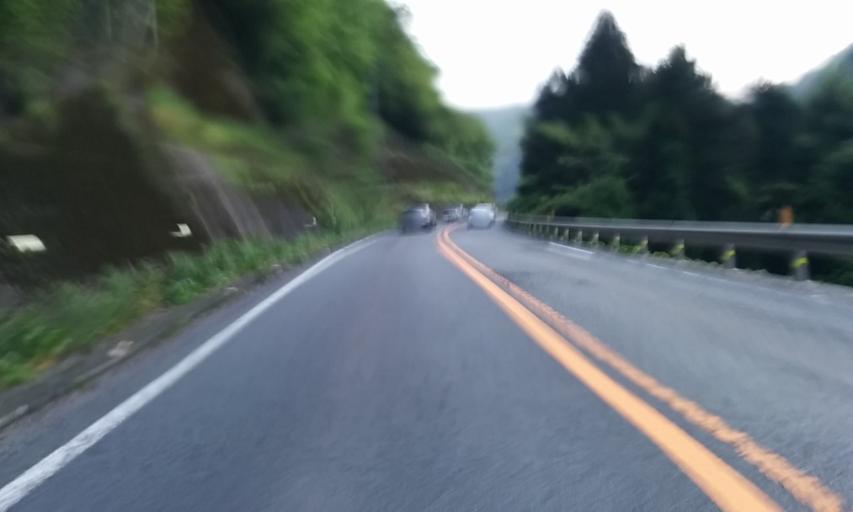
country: JP
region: Ehime
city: Saijo
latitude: 33.8416
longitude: 132.9931
